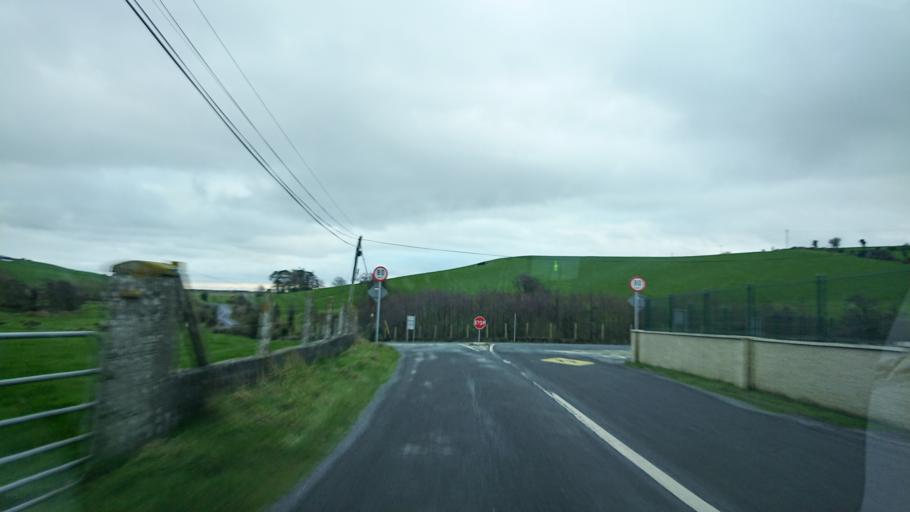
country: IE
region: Munster
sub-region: Waterford
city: Portlaw
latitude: 52.1541
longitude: -7.3827
